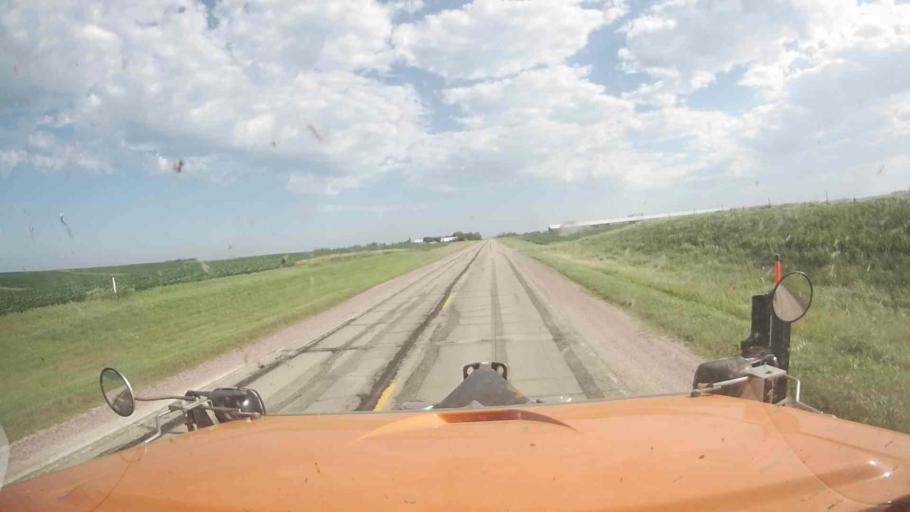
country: US
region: Iowa
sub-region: Osceola County
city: Sibley
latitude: 43.4673
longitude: -95.6432
